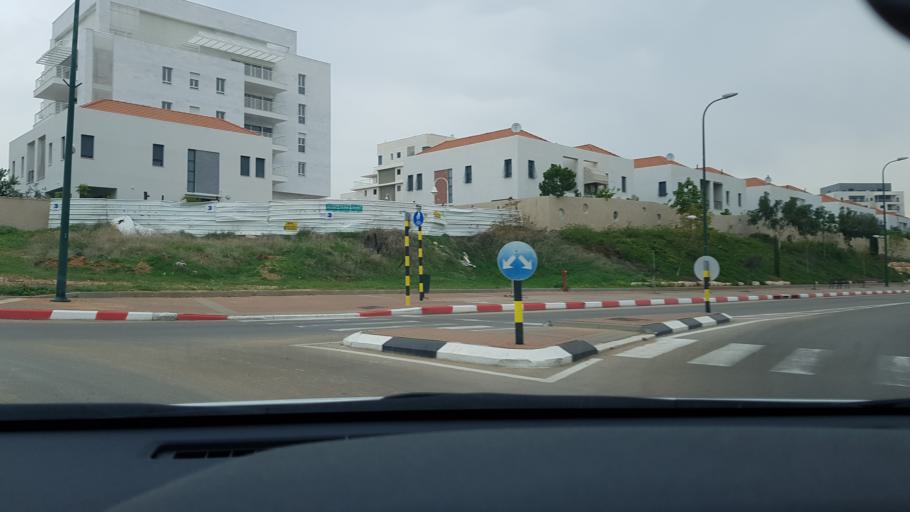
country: IL
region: Central District
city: Ness Ziona
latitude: 31.9210
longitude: 34.8049
